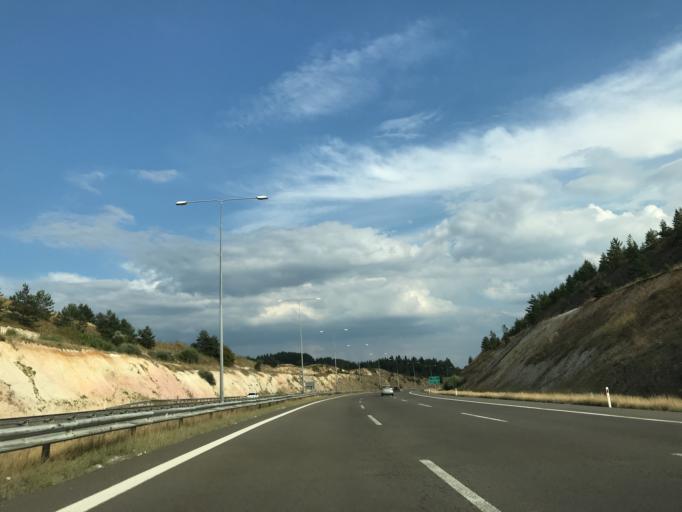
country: TR
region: Ankara
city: Pecenek
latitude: 40.5783
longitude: 32.2973
